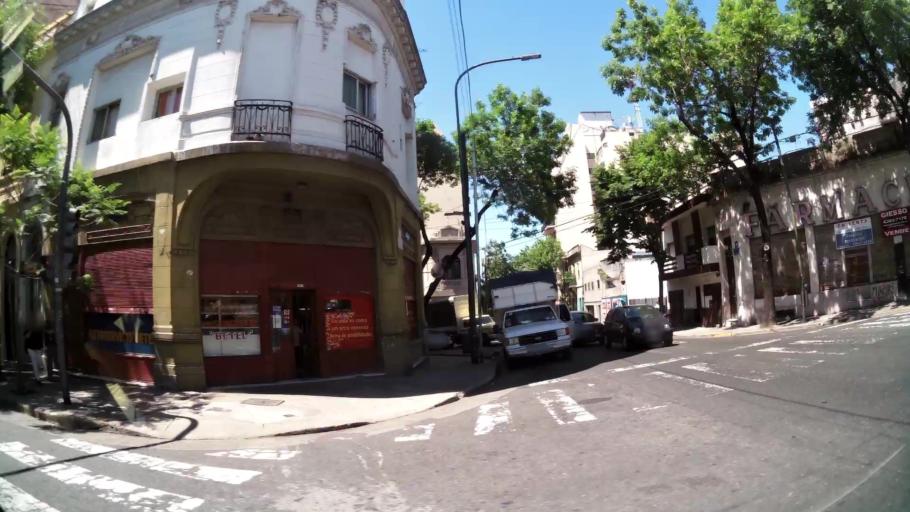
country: AR
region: Buenos Aires F.D.
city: Buenos Aires
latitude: -34.6281
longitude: -58.4066
